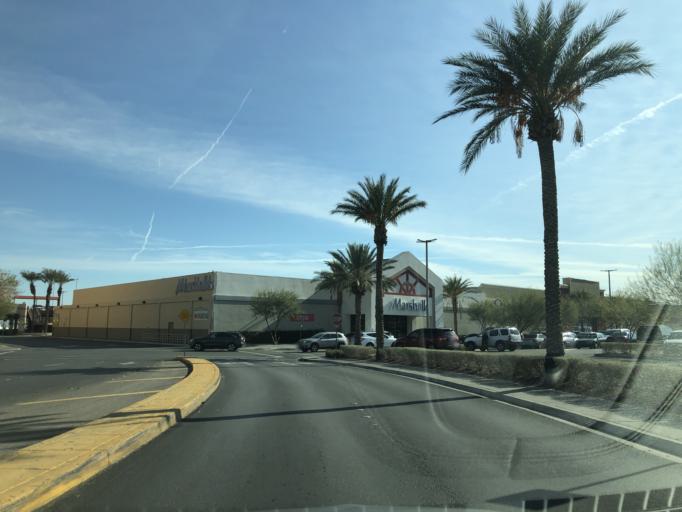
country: US
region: Nevada
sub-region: Clark County
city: Winchester
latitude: 36.1219
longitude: -115.1364
